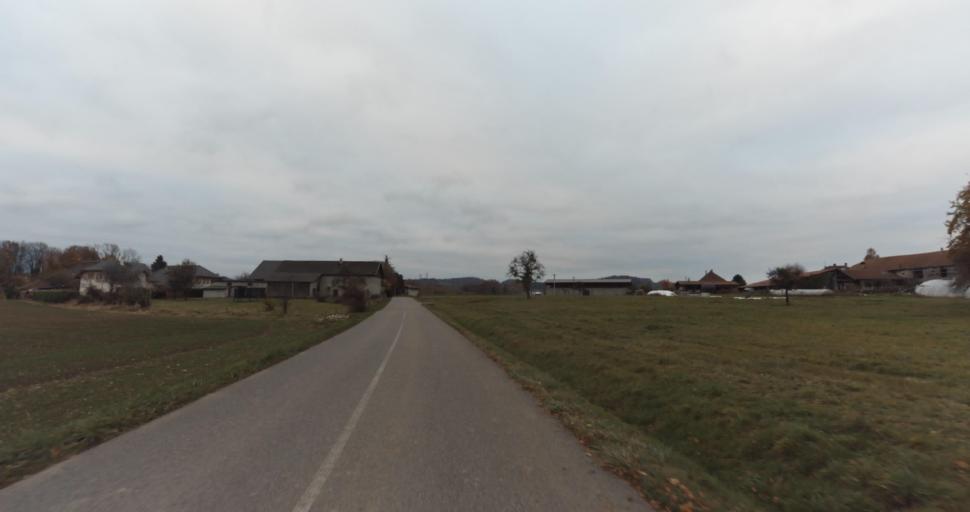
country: FR
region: Rhone-Alpes
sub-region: Departement de la Haute-Savoie
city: Chavanod
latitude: 45.8909
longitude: 6.0422
